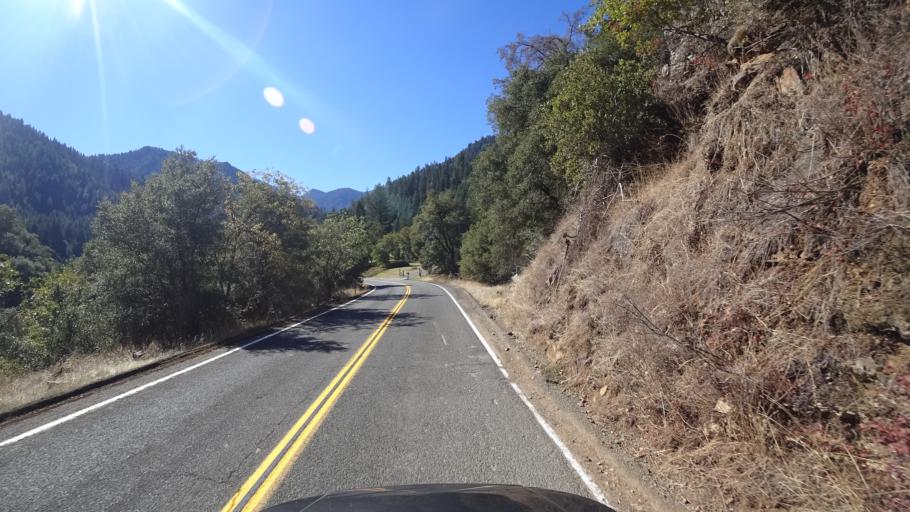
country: US
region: California
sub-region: Siskiyou County
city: Happy Camp
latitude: 41.3399
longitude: -123.4072
